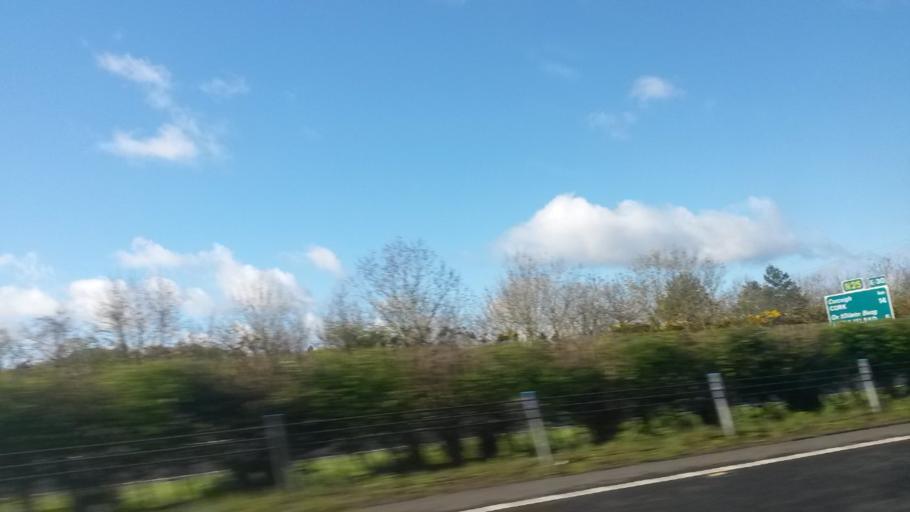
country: IE
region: Munster
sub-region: County Cork
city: Carrigtwohill
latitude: 51.9064
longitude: -8.2916
